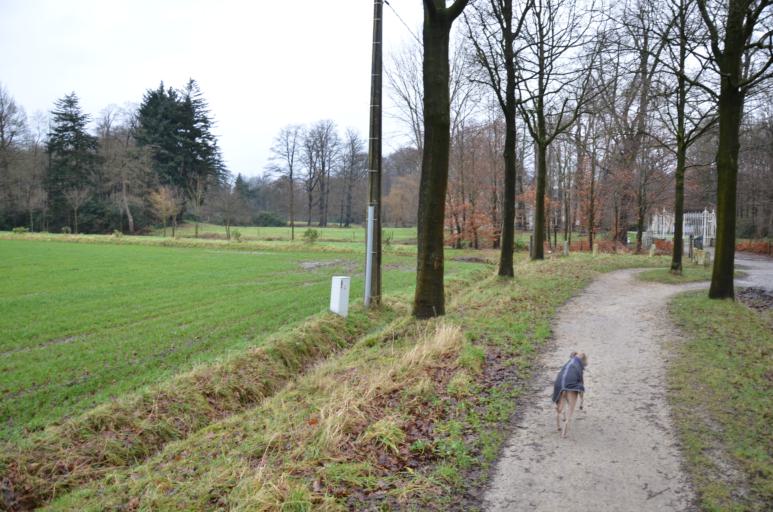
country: BE
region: Flanders
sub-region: Provincie Antwerpen
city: Oostmalle
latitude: 51.3045
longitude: 4.6942
